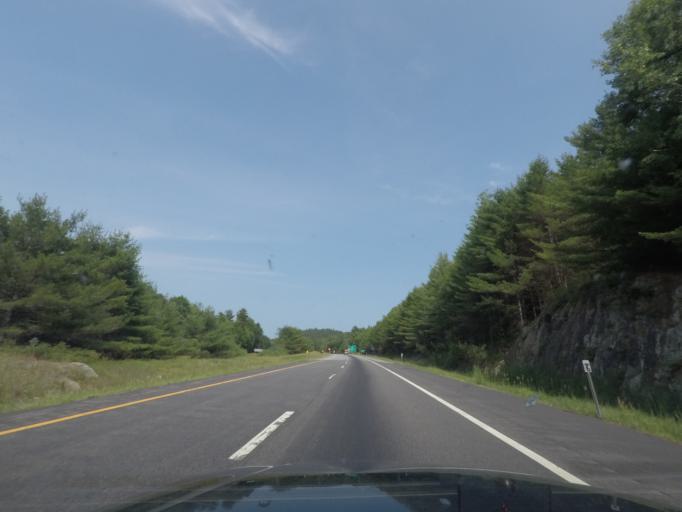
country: US
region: New York
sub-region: Essex County
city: Elizabethtown
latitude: 44.1971
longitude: -73.5250
